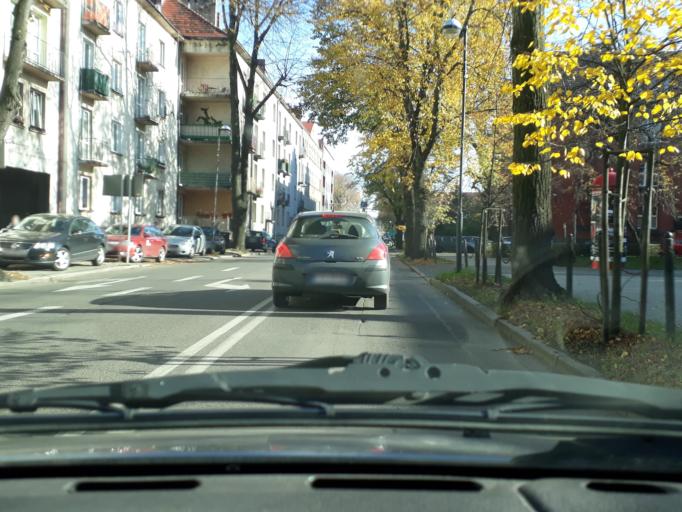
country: PL
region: Silesian Voivodeship
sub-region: Powiat tarnogorski
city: Tarnowskie Gory
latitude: 50.4460
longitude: 18.8573
